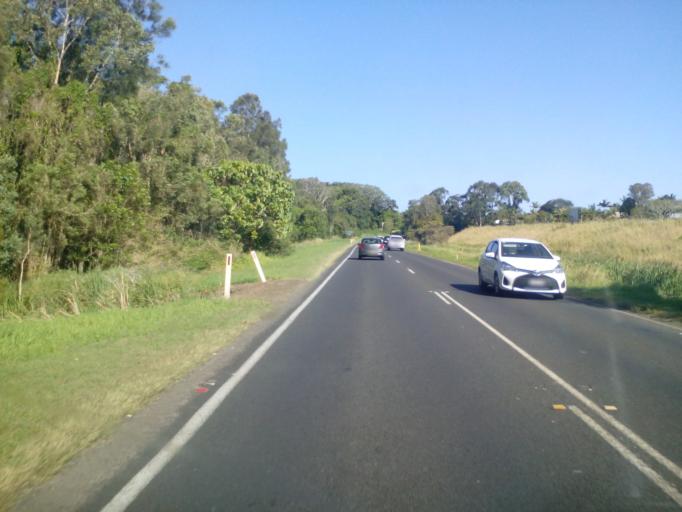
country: AU
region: New South Wales
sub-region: Tweed
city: Kingscliff
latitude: -28.2590
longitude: 153.5605
